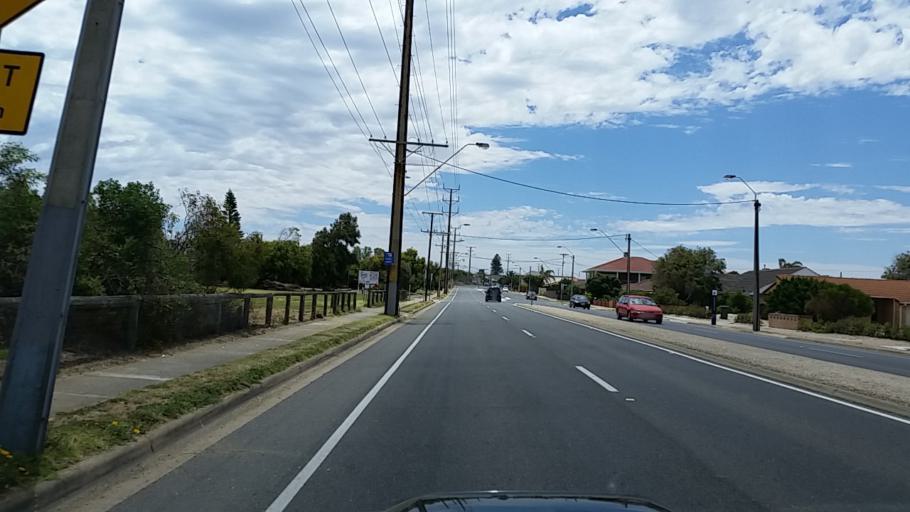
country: AU
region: South Australia
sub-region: Charles Sturt
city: West Lakes Shore
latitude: -34.8545
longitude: 138.4786
